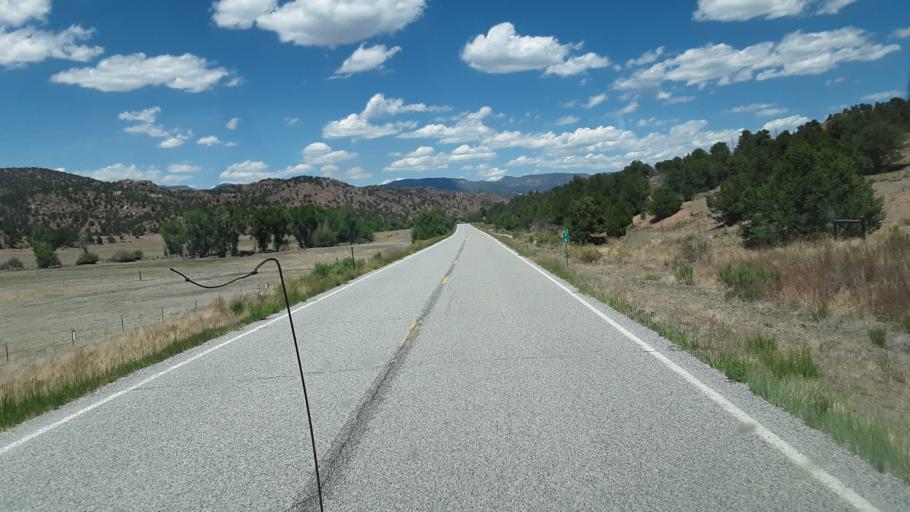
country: US
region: Colorado
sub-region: Custer County
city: Westcliffe
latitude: 38.3445
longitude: -105.5951
